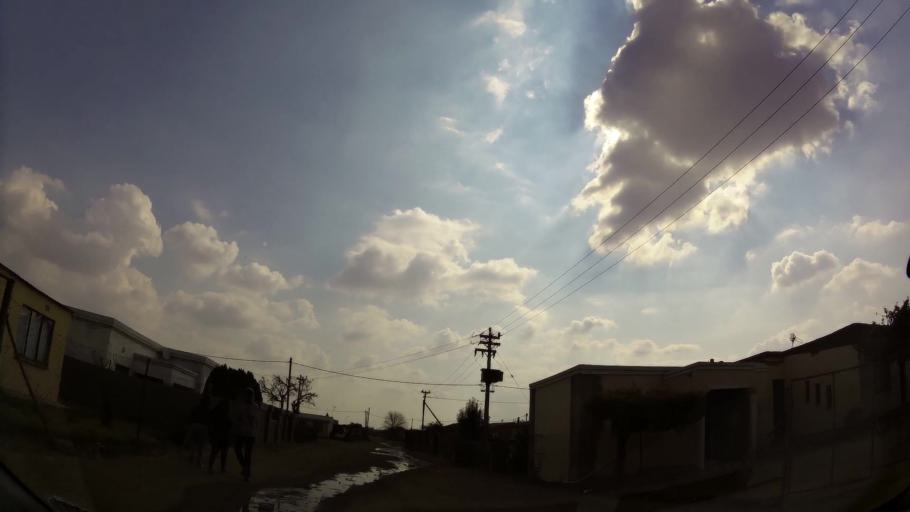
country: ZA
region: Gauteng
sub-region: Ekurhuleni Metropolitan Municipality
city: Springs
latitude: -26.1282
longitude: 28.4785
